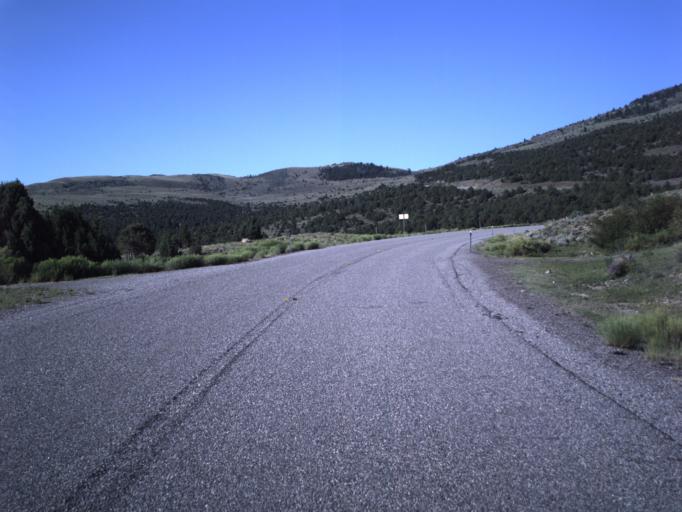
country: US
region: Utah
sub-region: Wayne County
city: Loa
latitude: 38.6204
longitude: -111.4551
